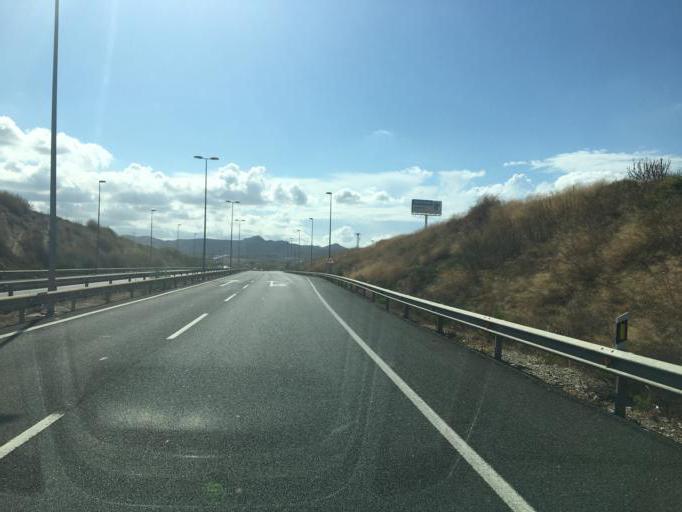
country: ES
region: Murcia
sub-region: Murcia
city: Cartagena
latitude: 37.6304
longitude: -0.9515
